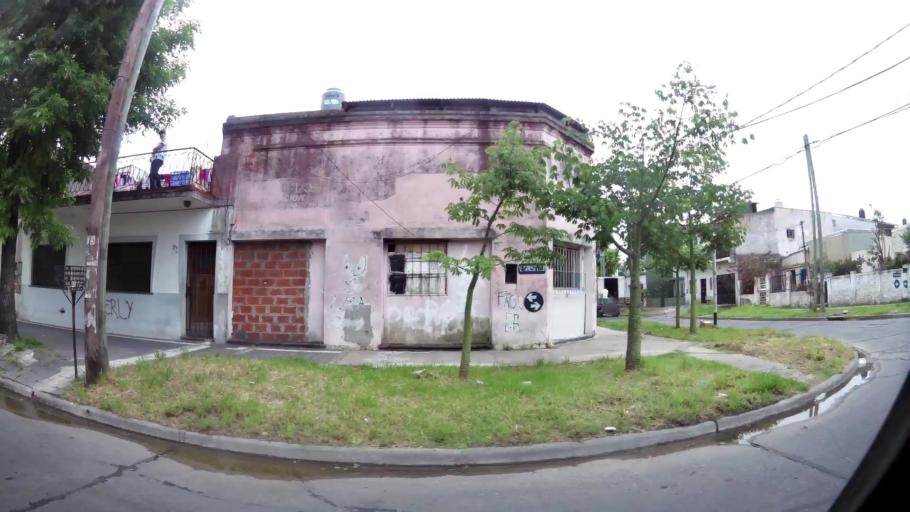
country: AR
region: Buenos Aires
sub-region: Partido de Avellaneda
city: Avellaneda
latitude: -34.6801
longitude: -58.3744
